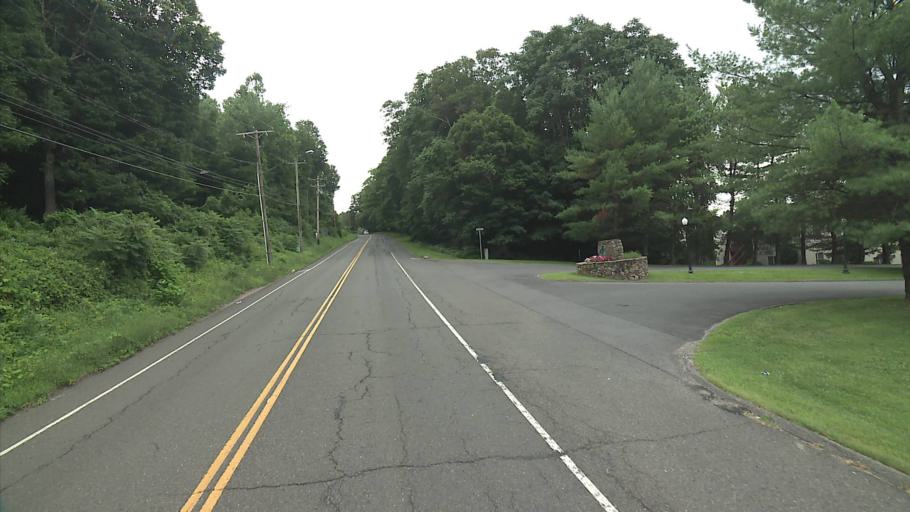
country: US
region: Connecticut
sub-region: Litchfield County
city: New Milford
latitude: 41.5718
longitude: -73.4029
